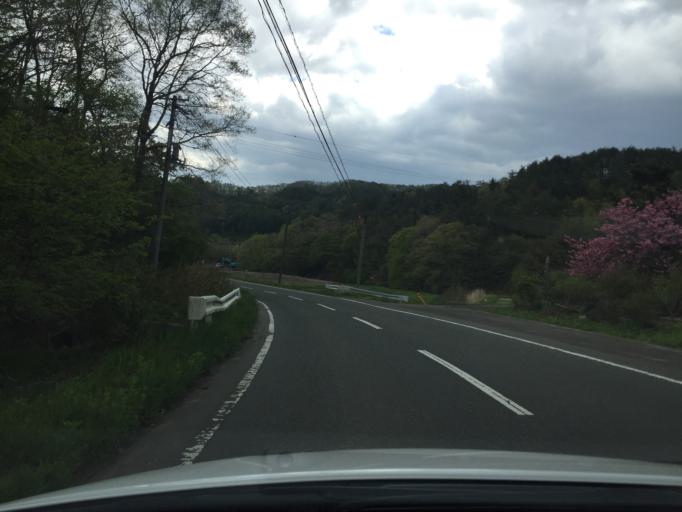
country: JP
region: Fukushima
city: Yanagawamachi-saiwaicho
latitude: 37.7403
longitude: 140.7259
